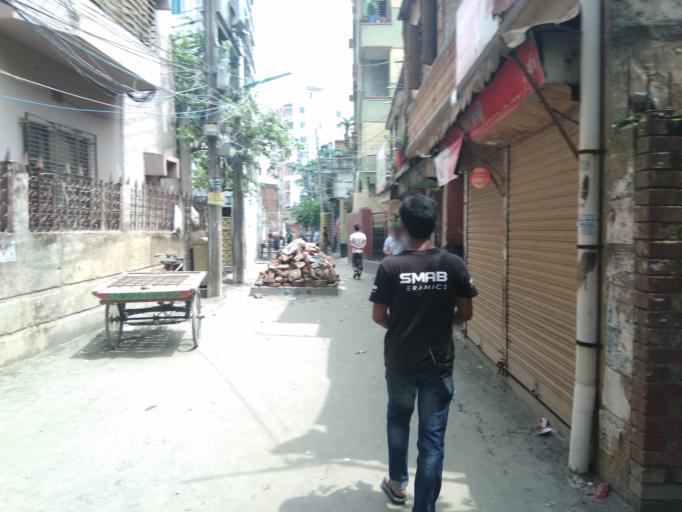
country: BD
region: Dhaka
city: Azimpur
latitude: 23.8020
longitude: 90.3677
